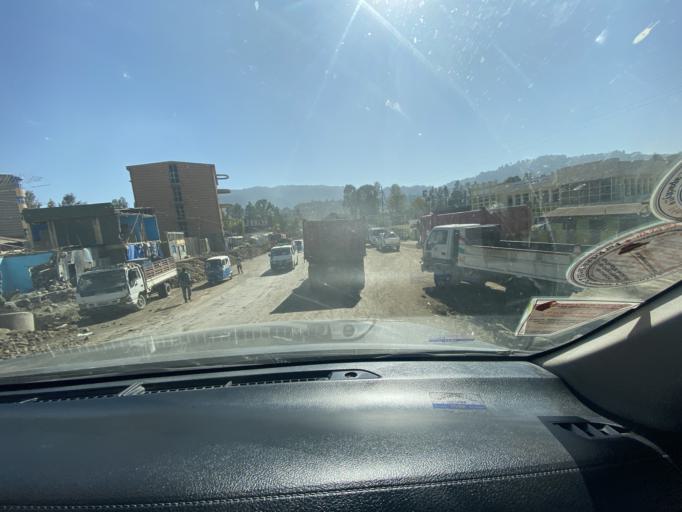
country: ET
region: Amhara
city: Robit
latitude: 11.8252
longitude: 39.5896
